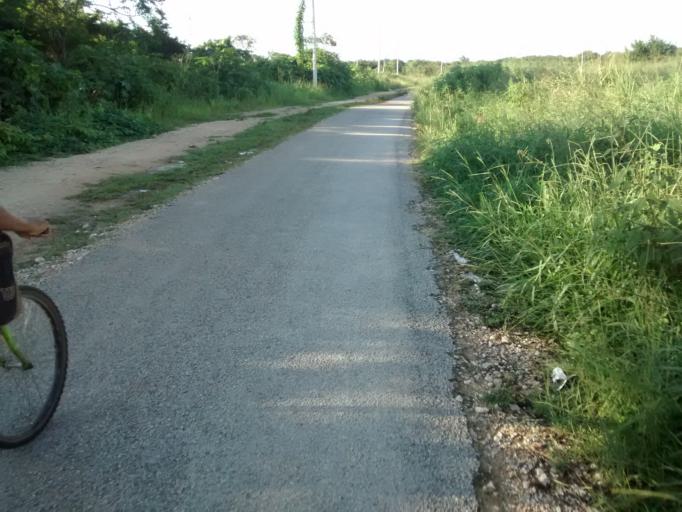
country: MX
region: Yucatan
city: Valladolid
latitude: 20.7066
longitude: -88.2151
